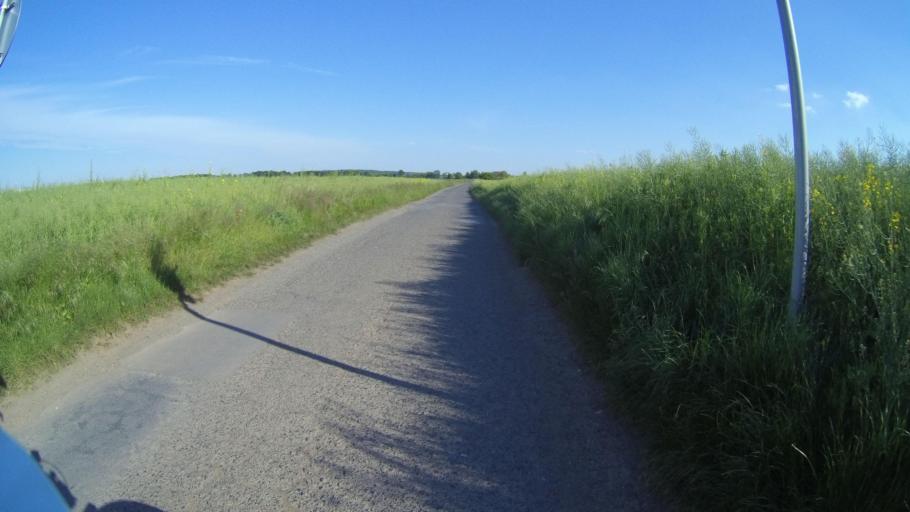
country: CZ
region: Central Bohemia
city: Zdiby
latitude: 50.1638
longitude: 14.4334
